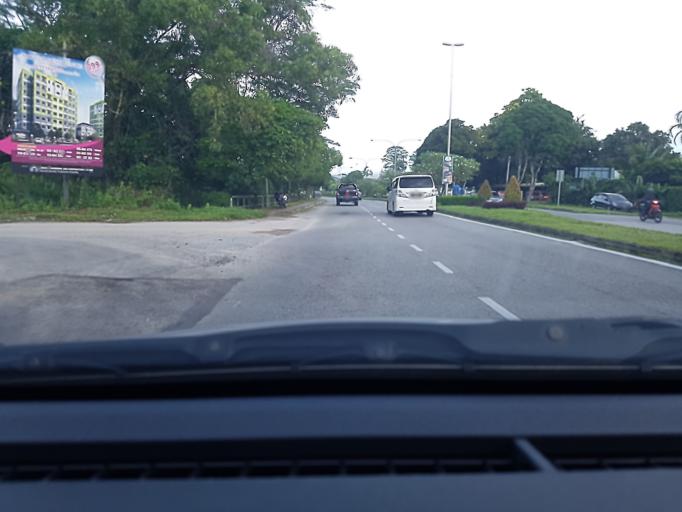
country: MY
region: Sarawak
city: Kuching
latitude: 1.5283
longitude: 110.3652
